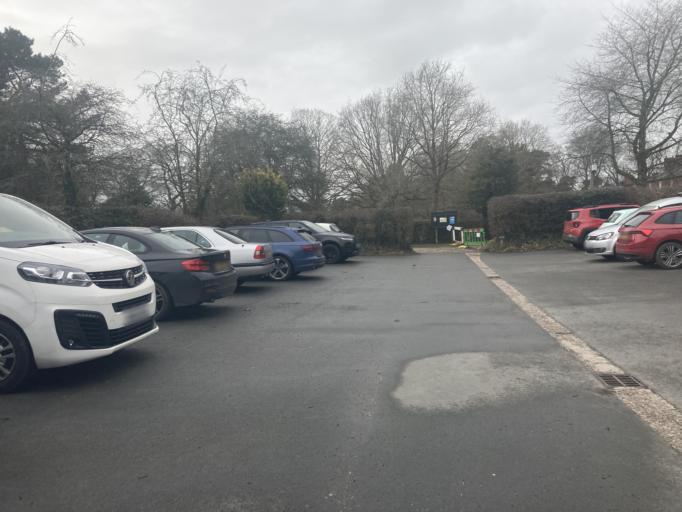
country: GB
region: England
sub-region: Cheshire East
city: Wilmslow
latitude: 53.3486
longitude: -2.2482
